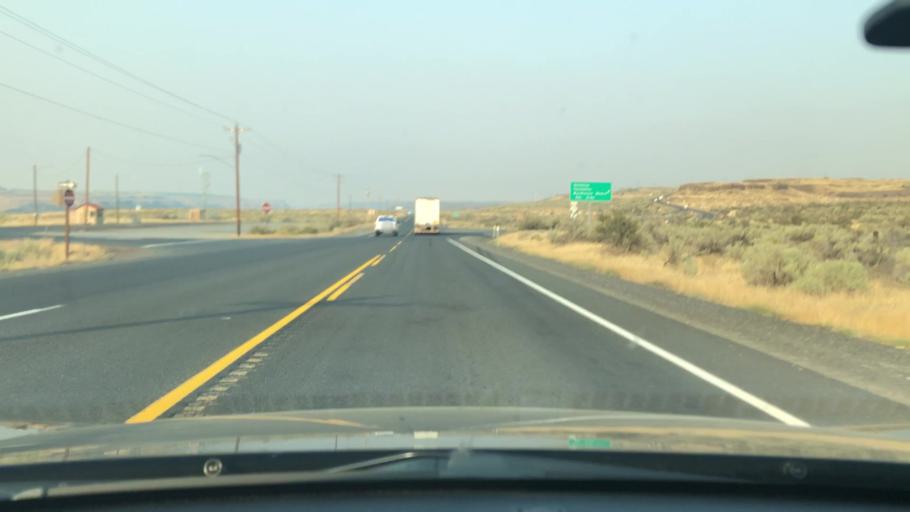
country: US
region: Oregon
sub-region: Umatilla County
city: Stanfield
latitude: 45.9134
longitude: -119.1396
